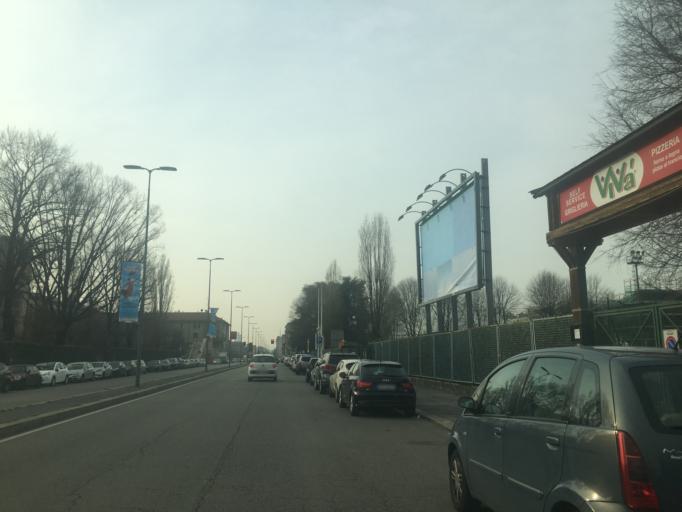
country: IT
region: Lombardy
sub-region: Citta metropolitana di Milano
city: Sesto San Giovanni
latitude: 45.5195
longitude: 9.2108
